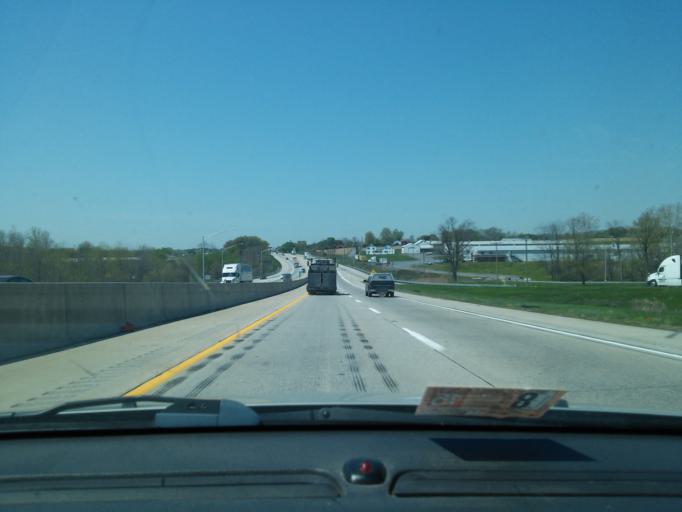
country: US
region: Pennsylvania
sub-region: Lebanon County
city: Fredericksburg
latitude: 40.4661
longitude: -76.3409
